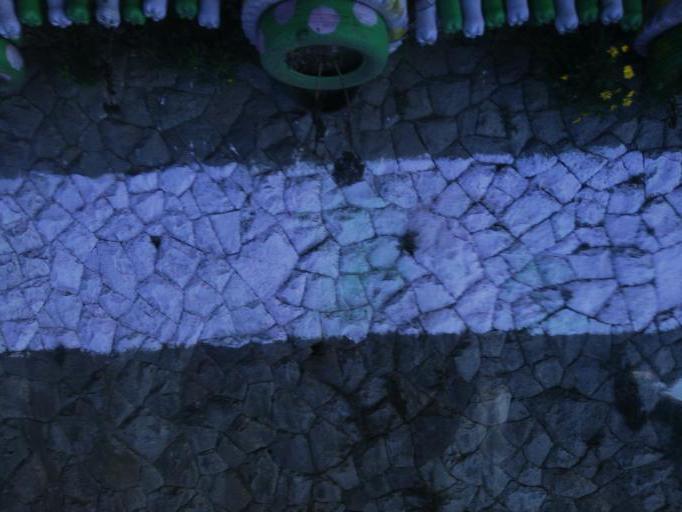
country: PH
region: Cordillera
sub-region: Baguio City
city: Baguio
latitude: 16.4321
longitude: 120.5971
